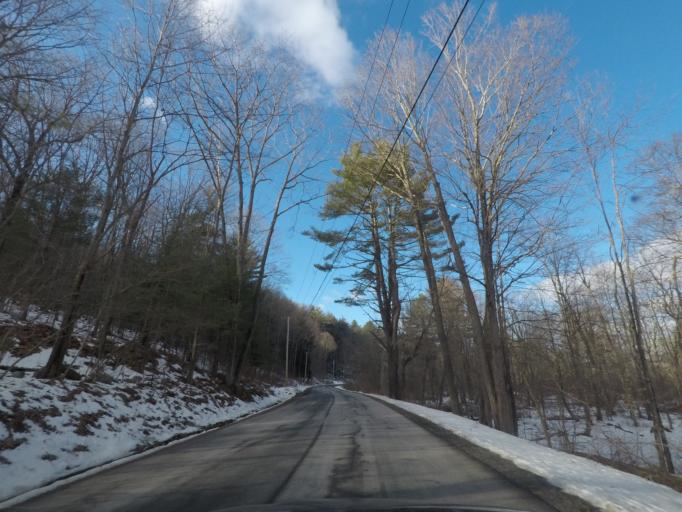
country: US
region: New York
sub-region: Rensselaer County
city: Nassau
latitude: 42.5354
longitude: -73.5286
